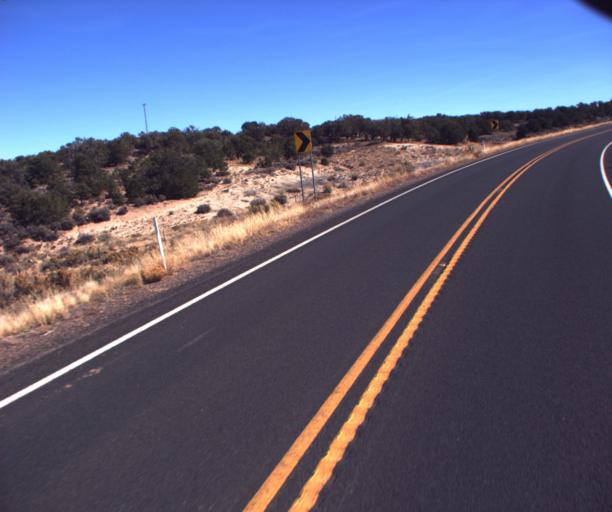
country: US
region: Arizona
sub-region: Apache County
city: Ganado
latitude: 35.7681
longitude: -109.7942
